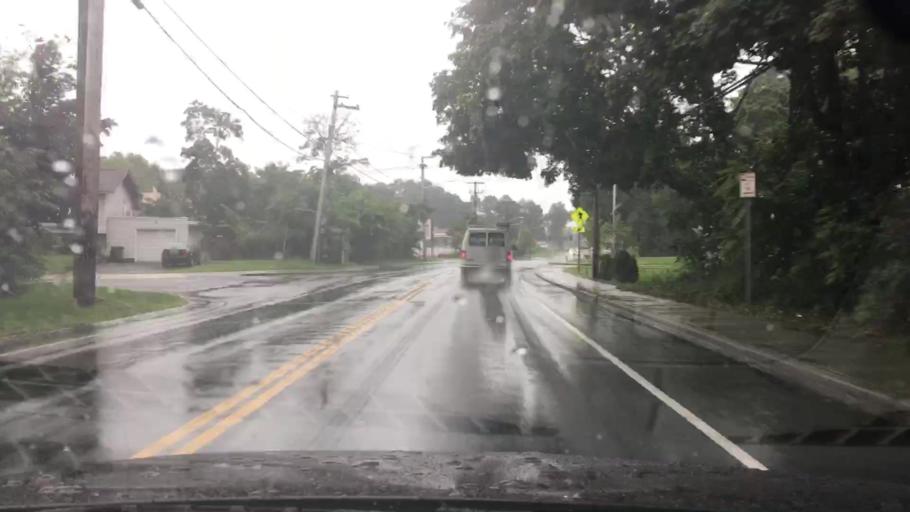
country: US
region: New York
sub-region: Suffolk County
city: Hauppauge
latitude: 40.8333
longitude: -73.1959
